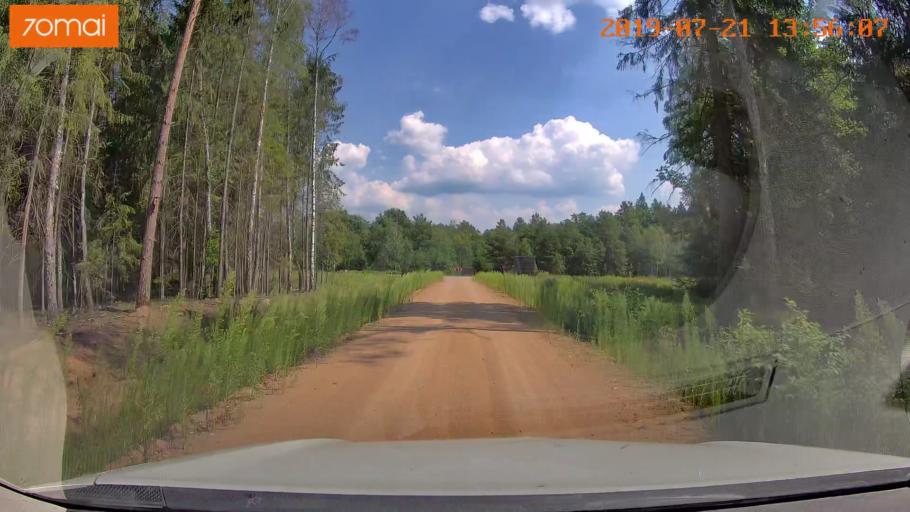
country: BY
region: Grodnenskaya
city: Lyubcha
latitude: 53.7809
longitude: 26.0986
